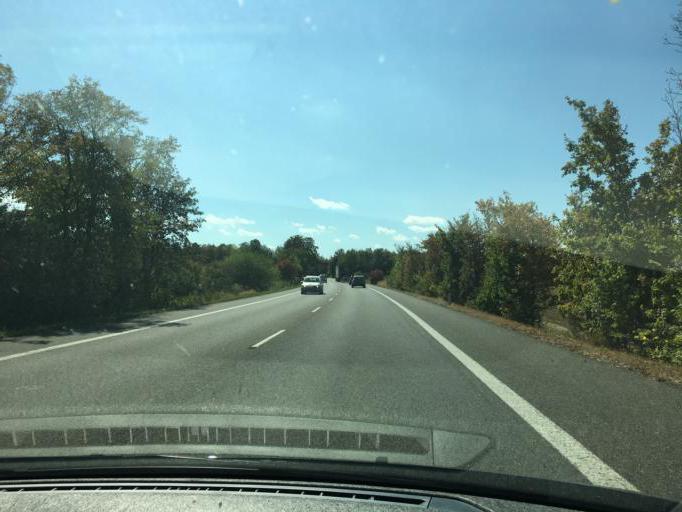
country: DE
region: North Rhine-Westphalia
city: Zulpich
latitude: 50.6963
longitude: 6.6379
